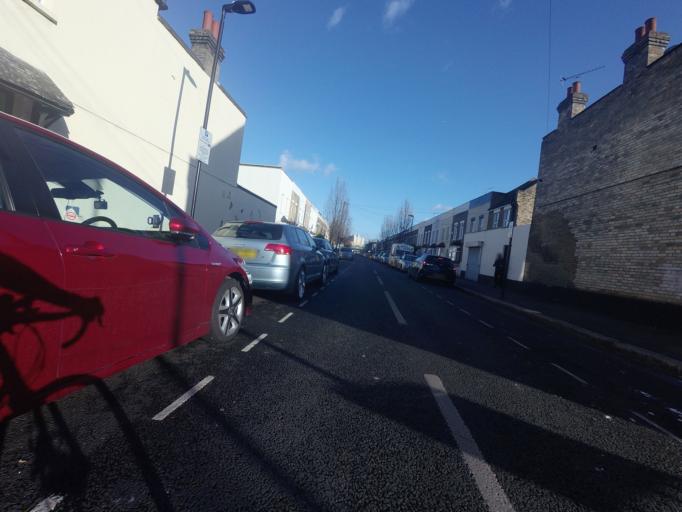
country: GB
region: England
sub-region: Greater London
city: East Ham
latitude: 51.5520
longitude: 0.0193
